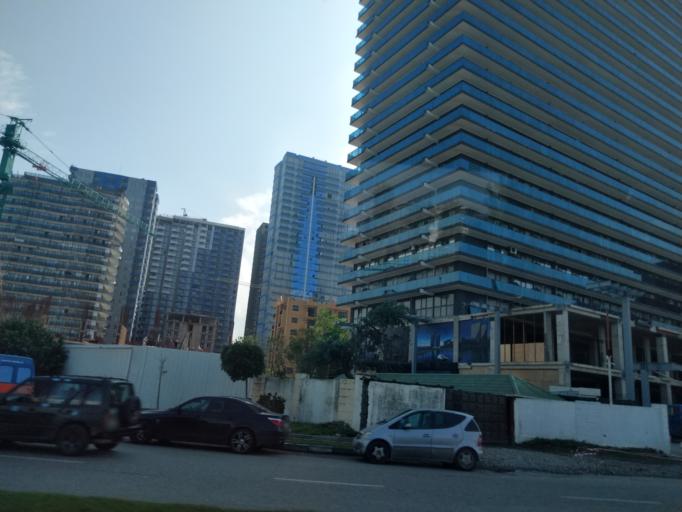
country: GE
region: Ajaria
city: Batumi
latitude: 41.6302
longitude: 41.6014
